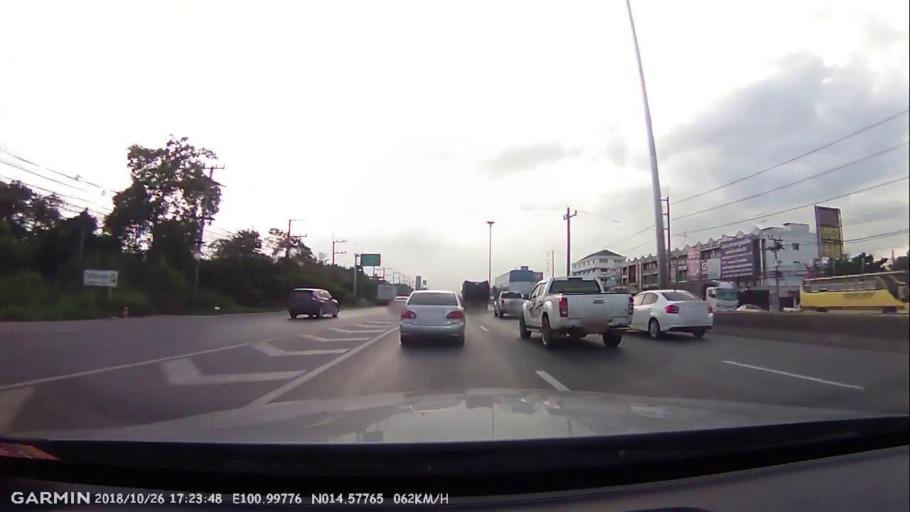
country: TH
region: Sara Buri
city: Kaeng Khoi
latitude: 14.5772
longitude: 100.9978
